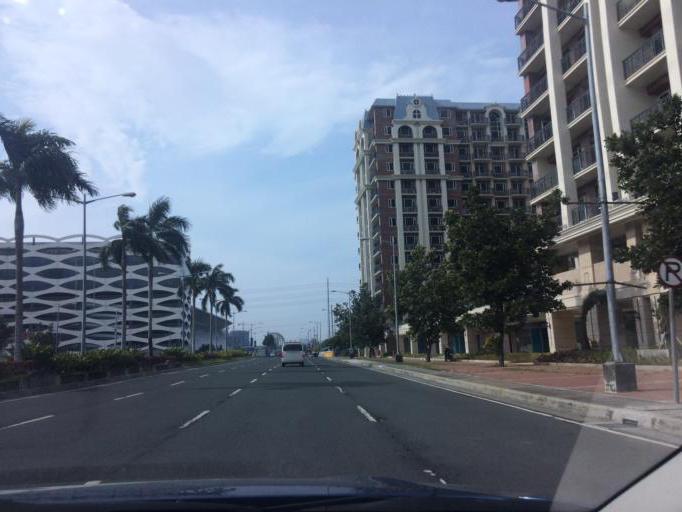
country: PH
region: Metro Manila
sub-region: Makati City
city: Makati City
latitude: 14.5288
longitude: 120.9849
